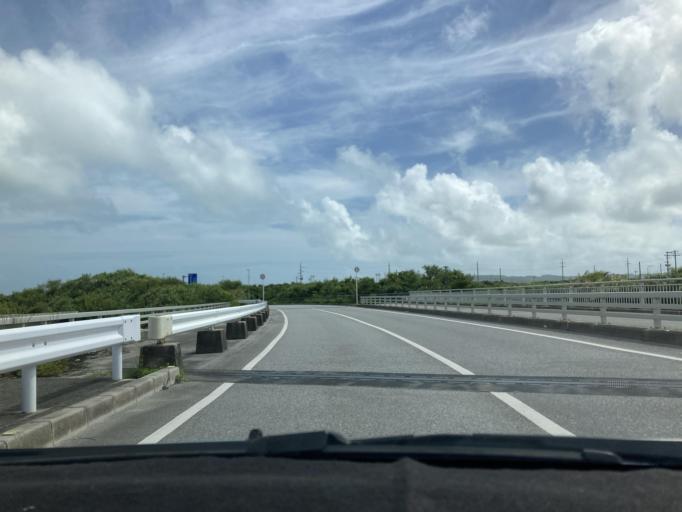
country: JP
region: Okinawa
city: Ginowan
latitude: 26.2112
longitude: 127.7626
